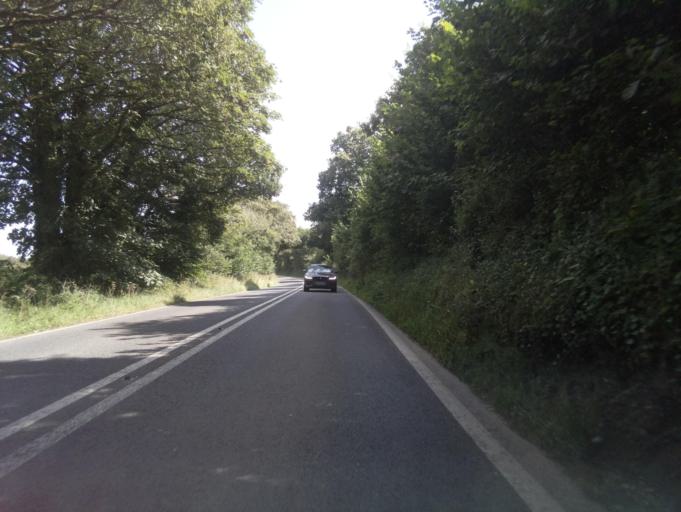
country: GB
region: England
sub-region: Cornwall
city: Saltash
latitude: 50.4272
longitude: -4.2540
